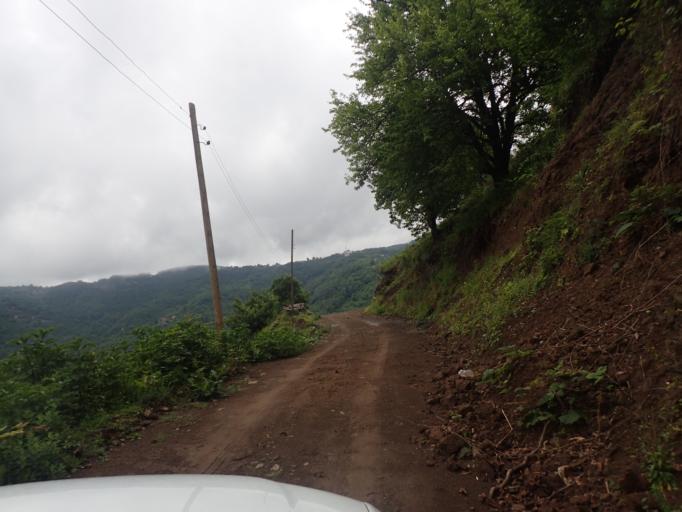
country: TR
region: Samsun
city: Salipazari
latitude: 40.9431
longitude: 36.8870
